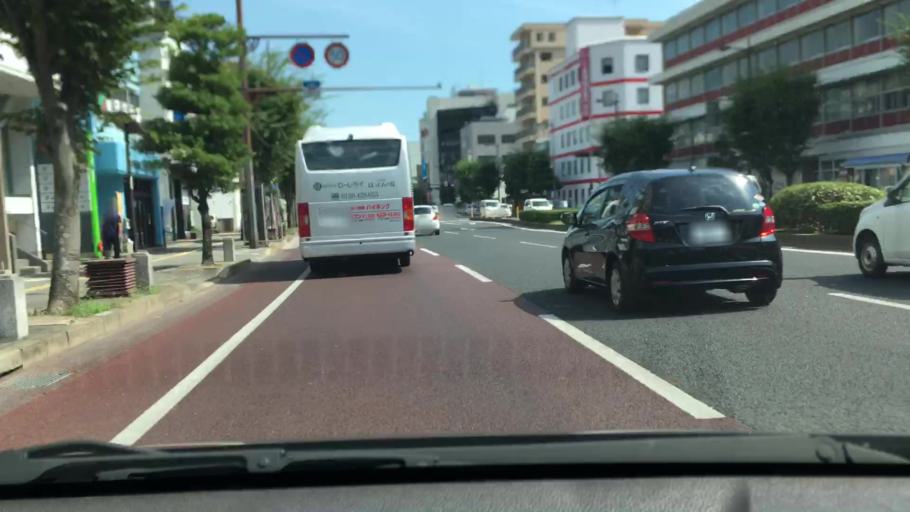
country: JP
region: Nagasaki
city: Sasebo
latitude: 33.1775
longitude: 129.7170
